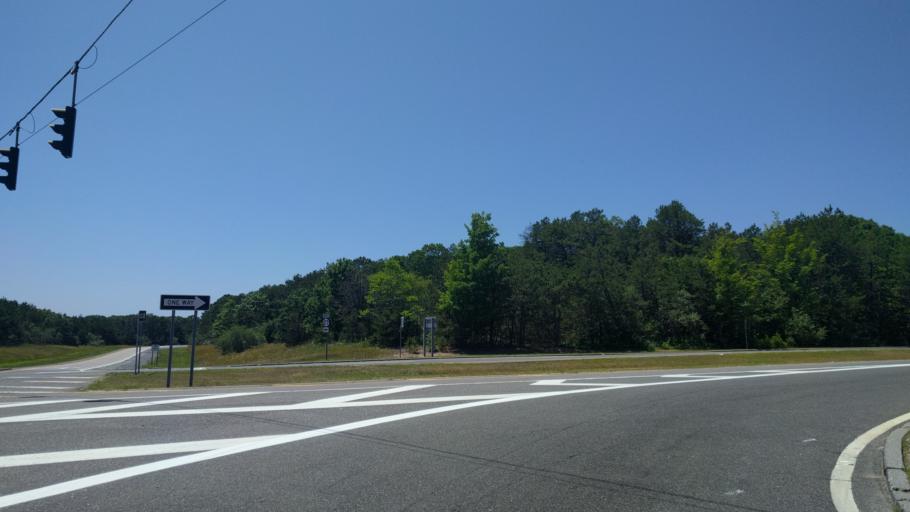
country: US
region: New York
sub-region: Suffolk County
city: Eastport
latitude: 40.8451
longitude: -72.7262
